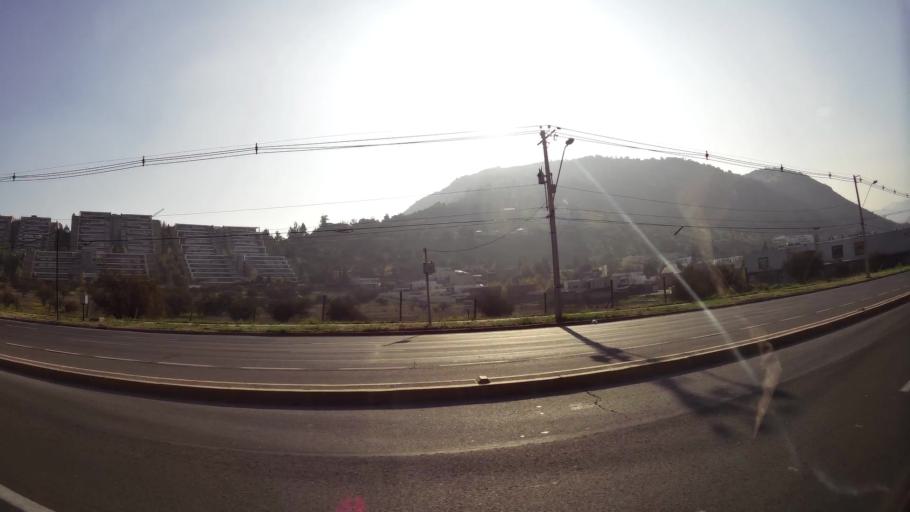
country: CL
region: Santiago Metropolitan
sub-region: Provincia de Santiago
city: Villa Presidente Frei, Nunoa, Santiago, Chile
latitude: -33.3628
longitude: -70.5444
